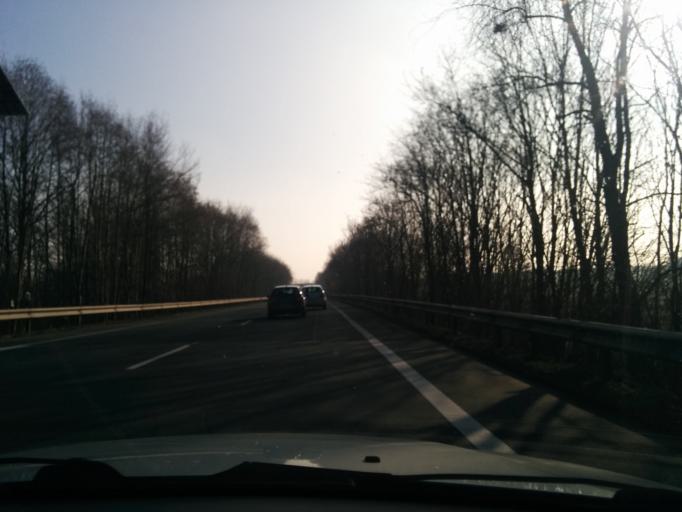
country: DE
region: North Rhine-Westphalia
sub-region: Regierungsbezirk Detmold
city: Blomberg
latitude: 51.9705
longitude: 9.0263
